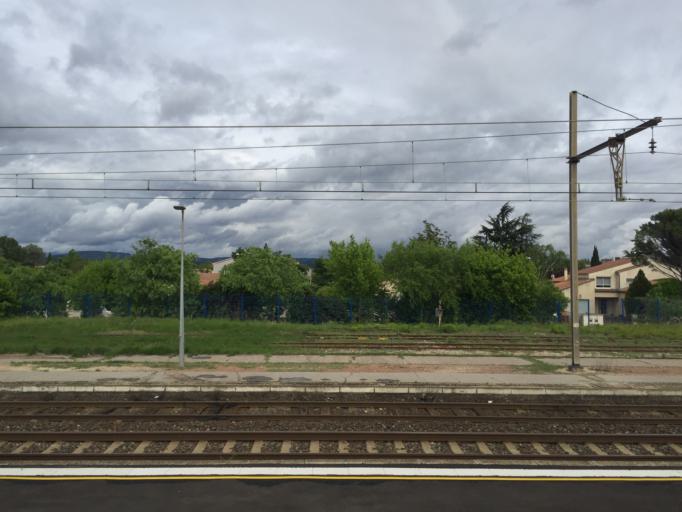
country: FR
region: Rhone-Alpes
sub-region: Departement de la Drome
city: Pierrelatte
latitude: 44.3735
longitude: 4.7037
